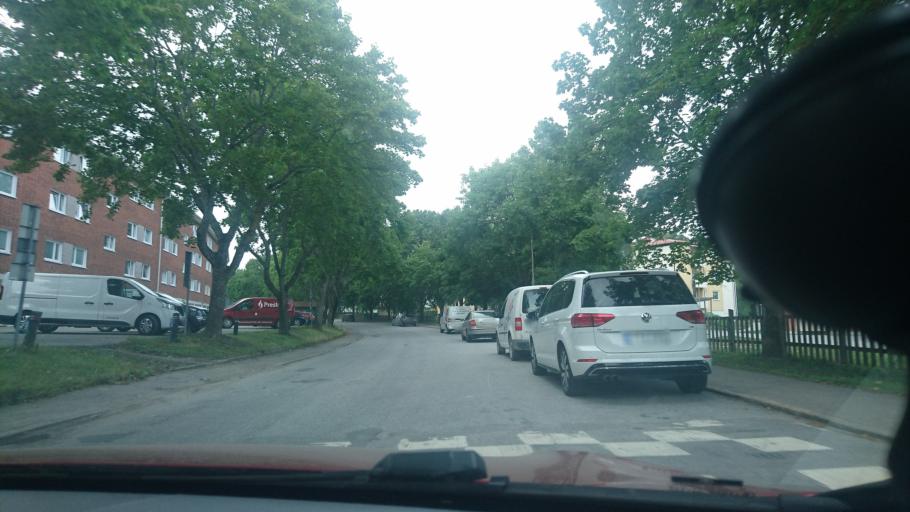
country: SE
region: Stockholm
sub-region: Upplands Vasby Kommun
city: Upplands Vaesby
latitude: 59.5218
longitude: 17.8951
